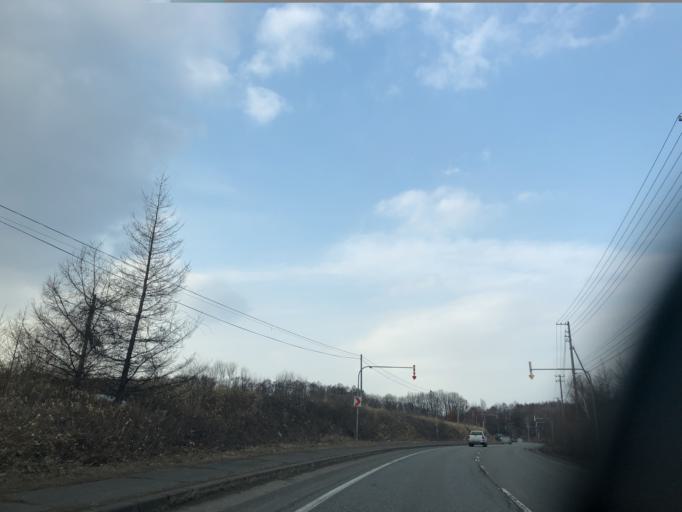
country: JP
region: Hokkaido
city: Chitose
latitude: 42.8030
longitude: 141.8343
